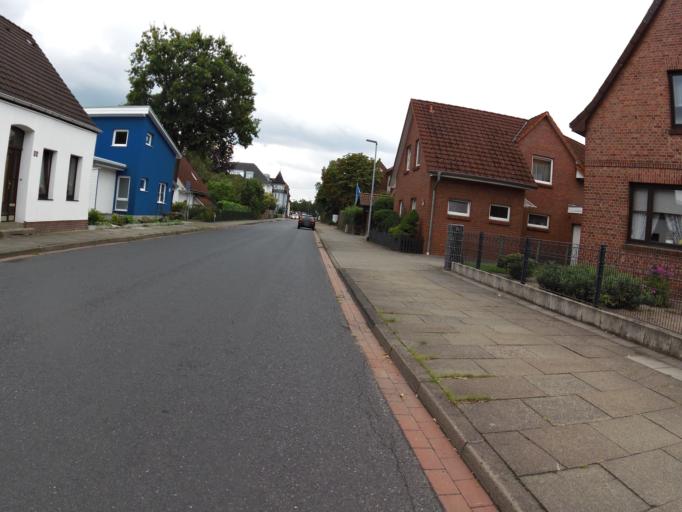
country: DE
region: Lower Saxony
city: Rotenburg
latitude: 53.1141
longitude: 9.4105
